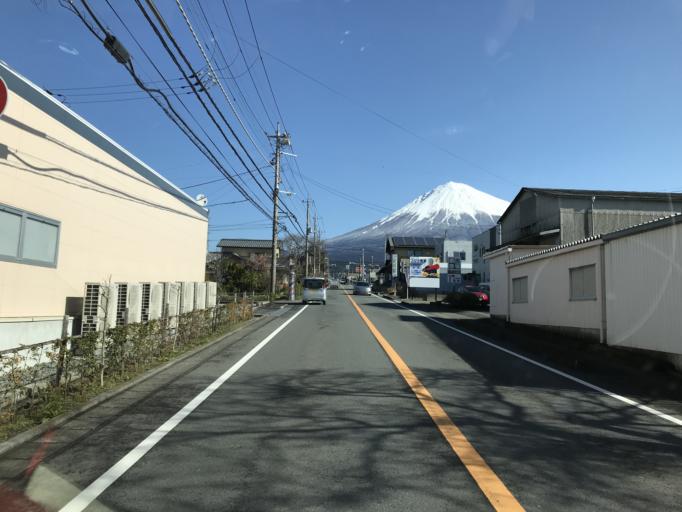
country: JP
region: Shizuoka
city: Fujinomiya
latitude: 35.2507
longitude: 138.6278
